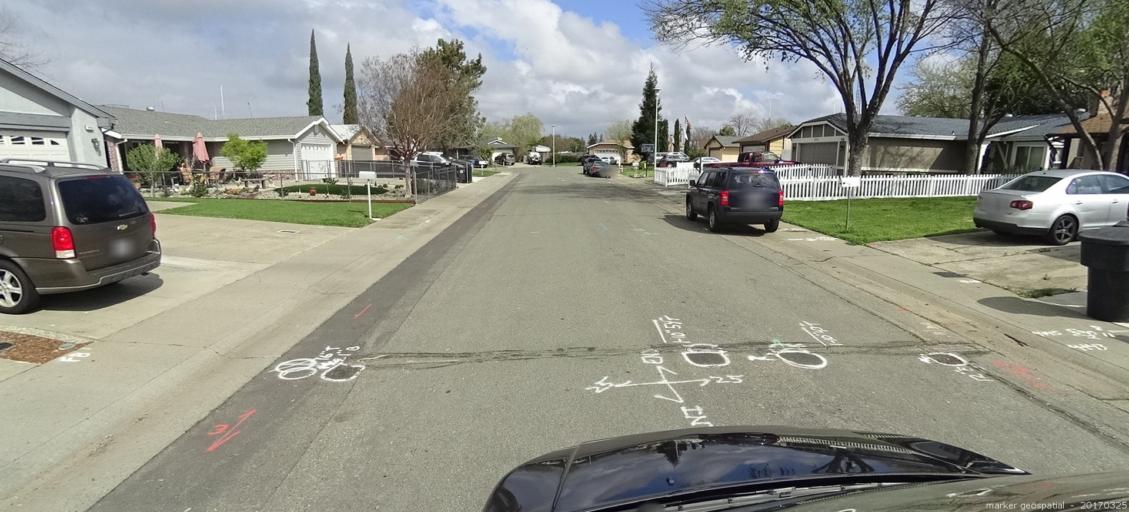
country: US
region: California
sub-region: Sacramento County
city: Florin
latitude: 38.5225
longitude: -121.4263
